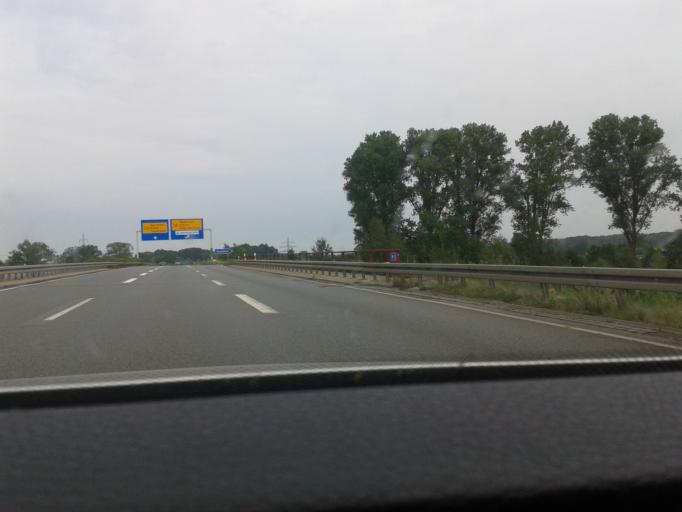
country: DE
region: Lower Saxony
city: Tappenbeck
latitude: 52.4600
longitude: 10.7371
